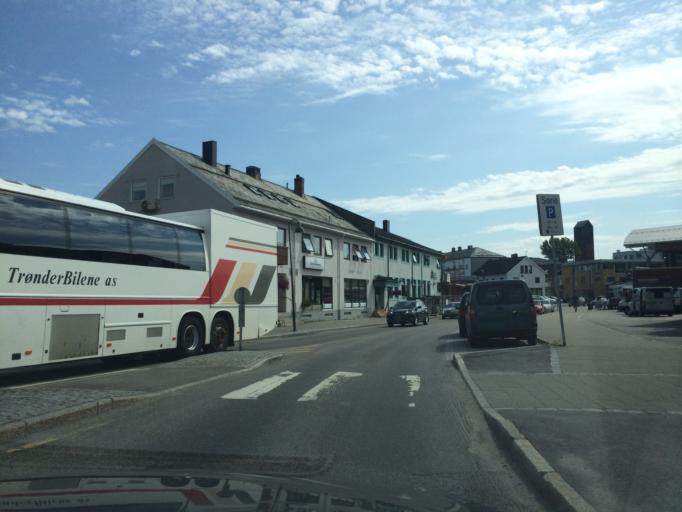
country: NO
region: Nord-Trondelag
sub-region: Namsos
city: Namsos
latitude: 64.4682
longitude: 11.4914
